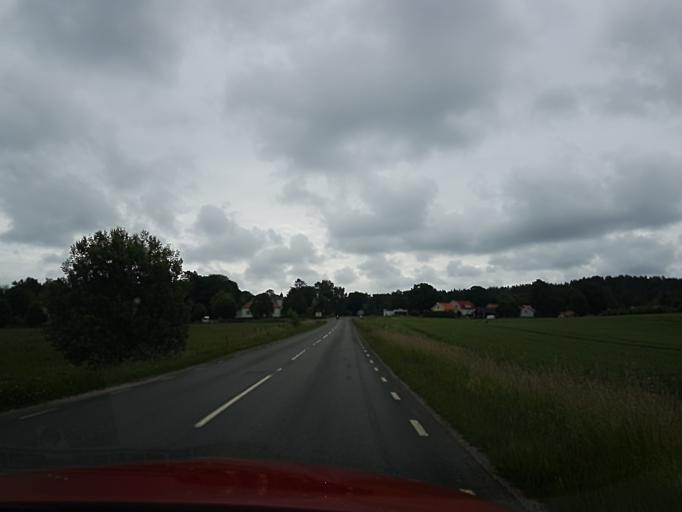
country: SE
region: Vaestra Goetaland
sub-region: Tidaholms Kommun
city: Olofstorp
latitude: 58.3049
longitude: 14.0924
